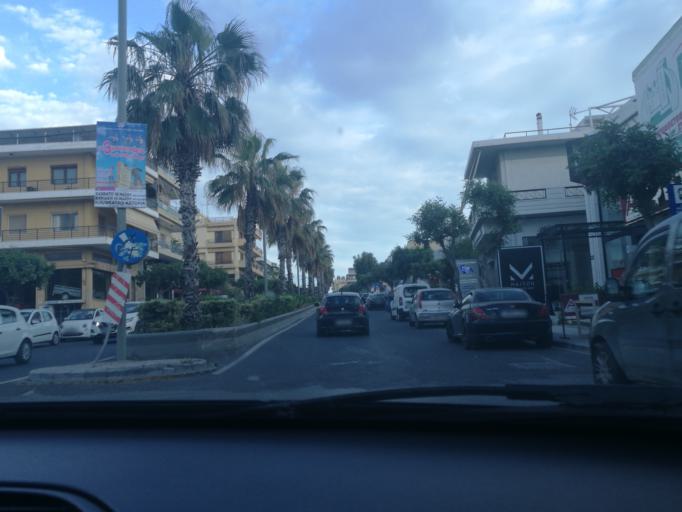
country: GR
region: Crete
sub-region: Nomos Irakleiou
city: Irakleion
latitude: 35.3198
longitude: 25.1441
